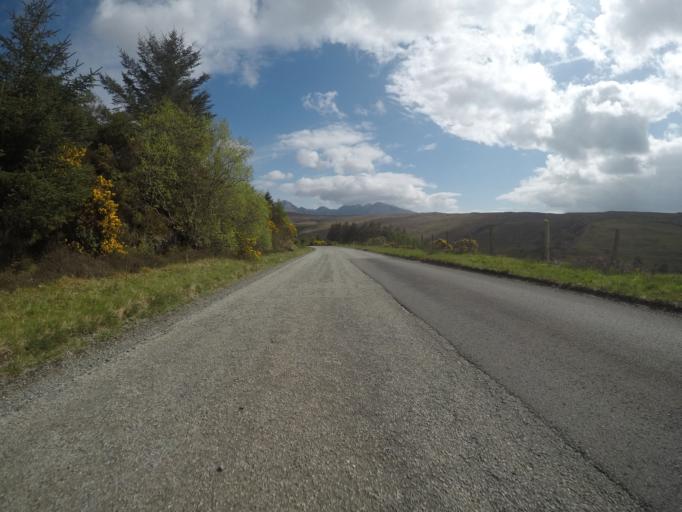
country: GB
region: Scotland
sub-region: Highland
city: Isle of Skye
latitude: 57.3006
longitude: -6.2957
